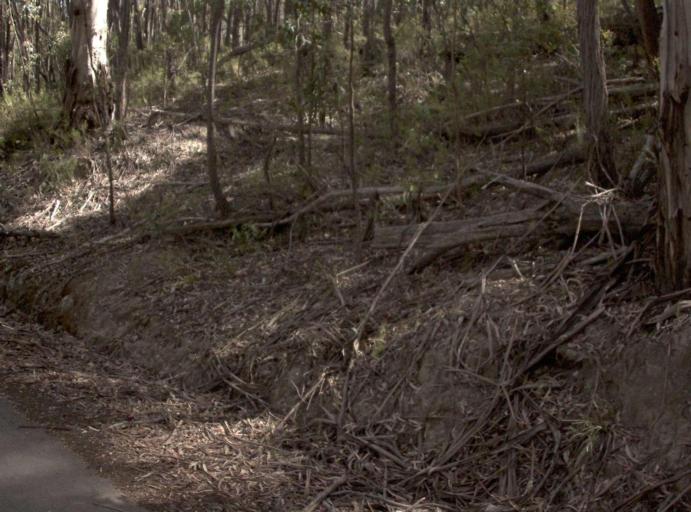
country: AU
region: Victoria
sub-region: East Gippsland
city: Lakes Entrance
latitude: -37.3928
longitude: 148.1232
